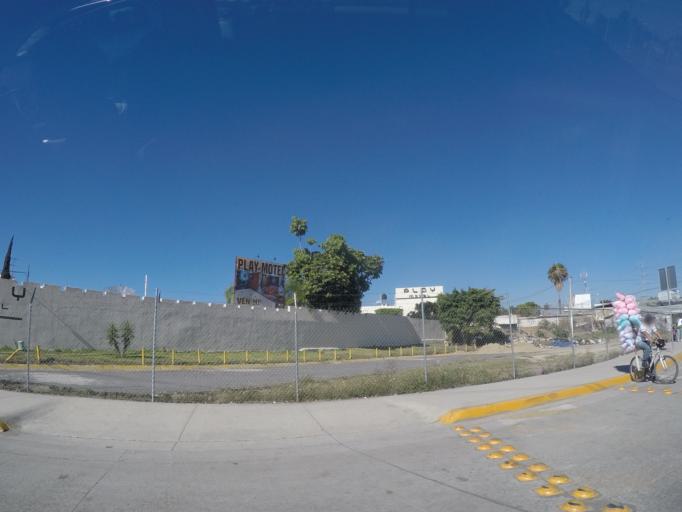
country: MX
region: Jalisco
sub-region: Zapopan
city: Zapopan
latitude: 20.7289
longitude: -103.3450
